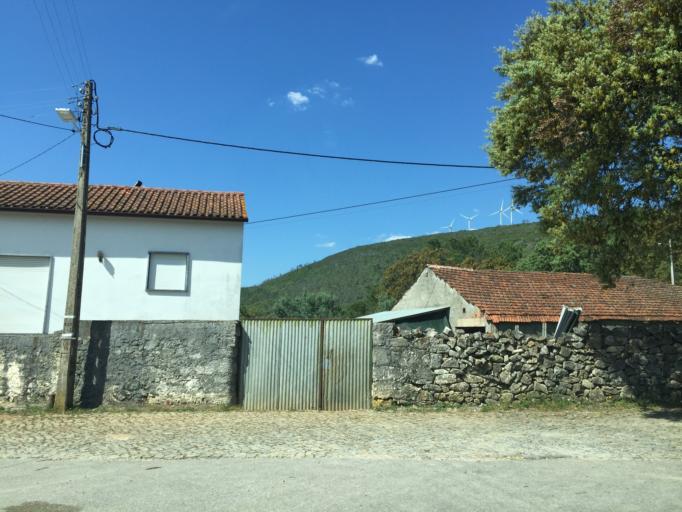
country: PT
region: Leiria
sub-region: Alvaiazere
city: Alvaiazere
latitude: 39.8093
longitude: -8.4264
